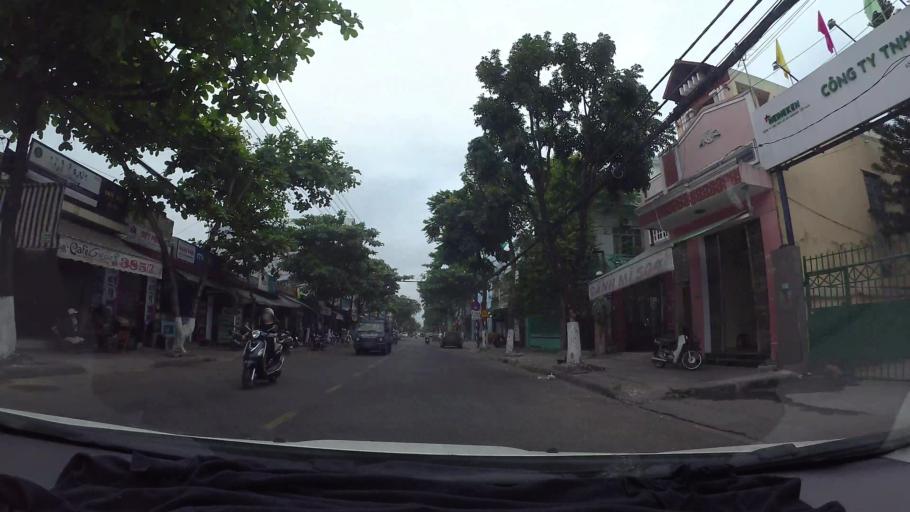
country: VN
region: Da Nang
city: Thanh Khe
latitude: 16.0712
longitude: 108.1955
